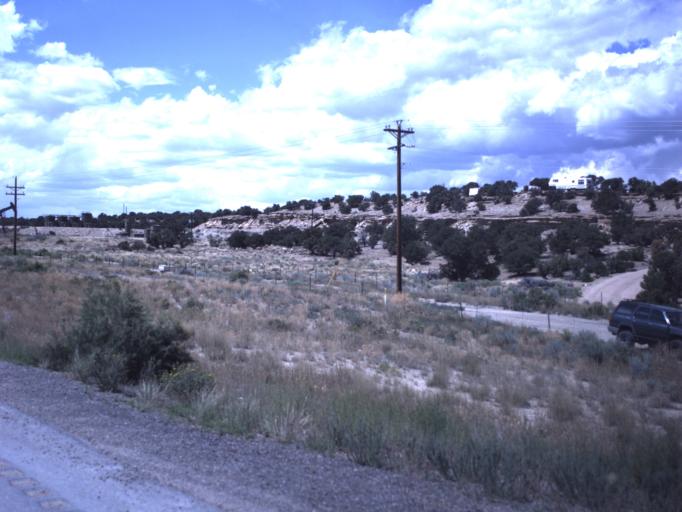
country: US
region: Utah
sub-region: Duchesne County
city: Duchesne
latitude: 40.1787
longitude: -110.5262
